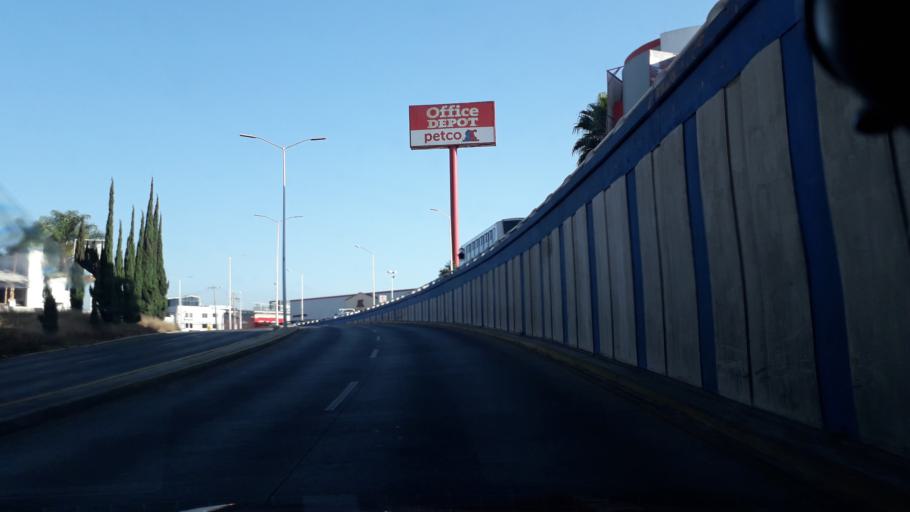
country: MX
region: Puebla
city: Puebla
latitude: 19.0384
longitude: -98.2255
